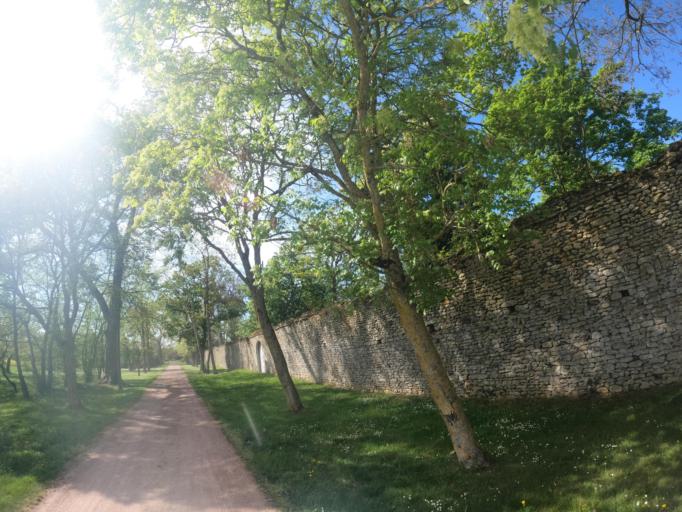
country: FR
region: Poitou-Charentes
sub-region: Departement des Deux-Sevres
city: Saint-Varent
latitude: 46.9251
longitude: -0.2184
